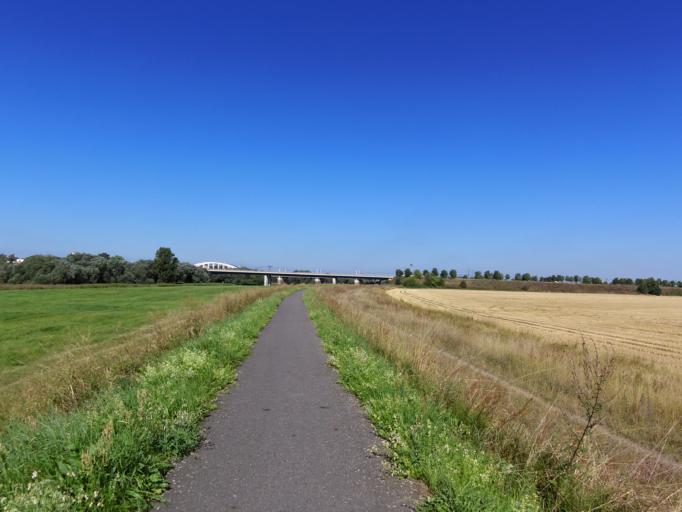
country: DE
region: Saxony
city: Riesa
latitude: 51.3096
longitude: 13.3031
